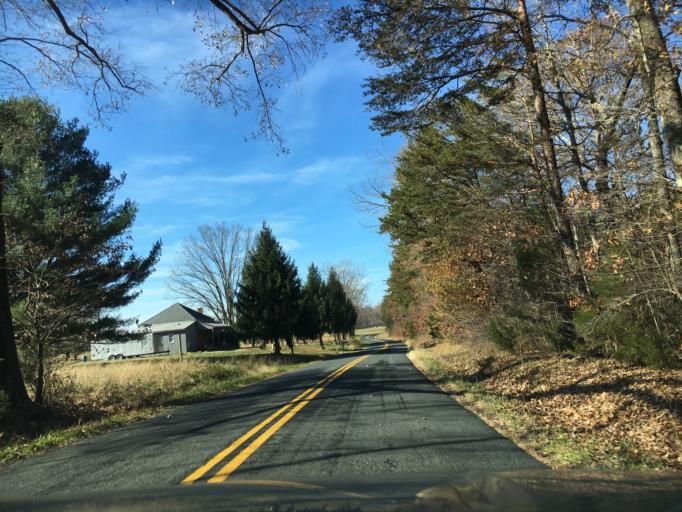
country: US
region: Virginia
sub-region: Buckingham County
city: Buckingham
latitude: 37.4327
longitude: -78.6238
